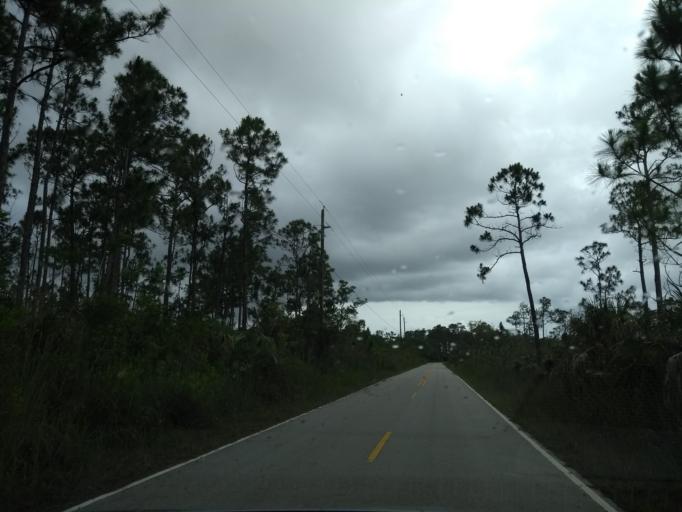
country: US
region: Florida
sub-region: Miami-Dade County
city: The Hammocks
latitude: 25.7480
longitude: -80.9380
